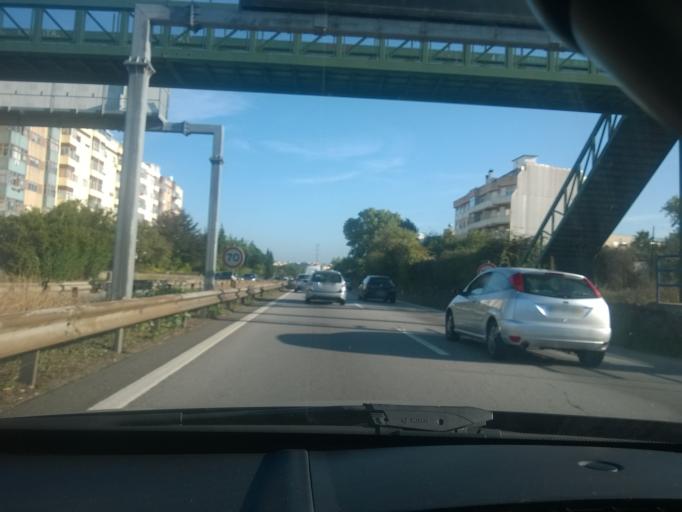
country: PT
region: Porto
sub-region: Matosinhos
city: Senhora da Hora
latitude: 41.1882
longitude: -8.6261
